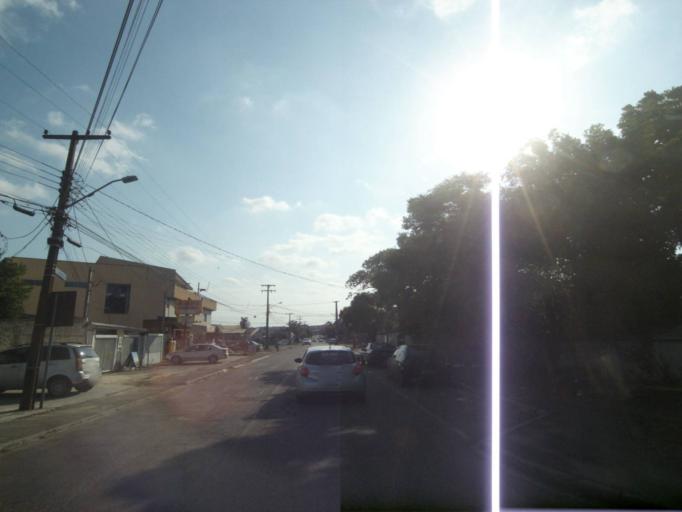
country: BR
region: Parana
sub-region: Curitiba
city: Curitiba
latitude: -25.4805
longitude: -49.3318
